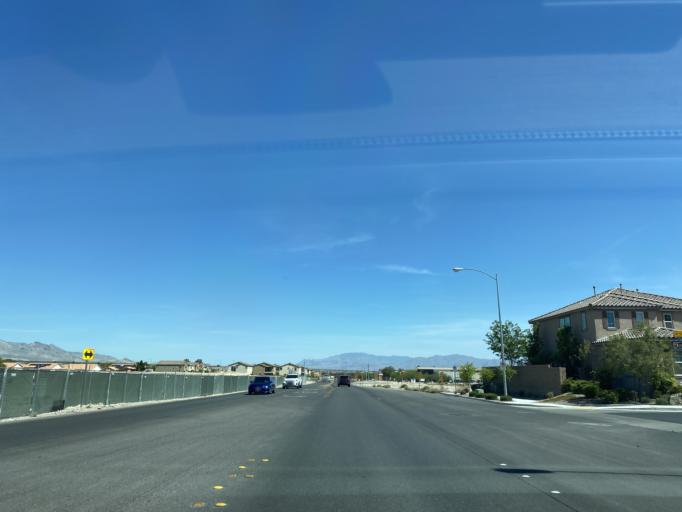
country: US
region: Nevada
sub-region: Clark County
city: Spring Valley
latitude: 36.0751
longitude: -115.2607
